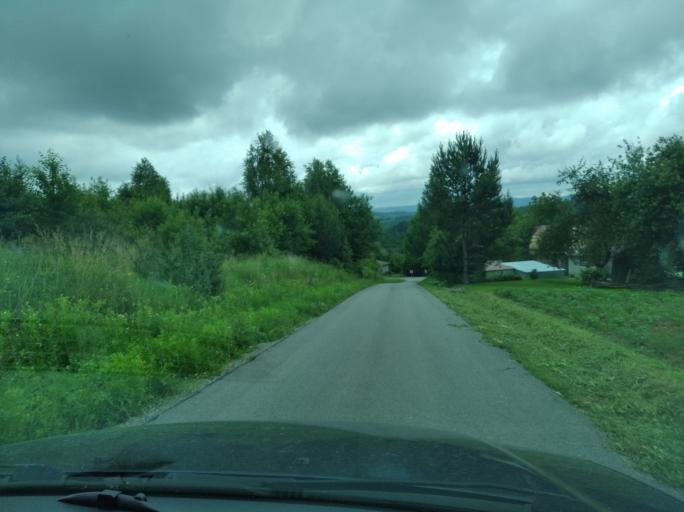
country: PL
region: Subcarpathian Voivodeship
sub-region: Powiat przemyski
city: Nienadowa
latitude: 49.8634
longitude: 22.4076
